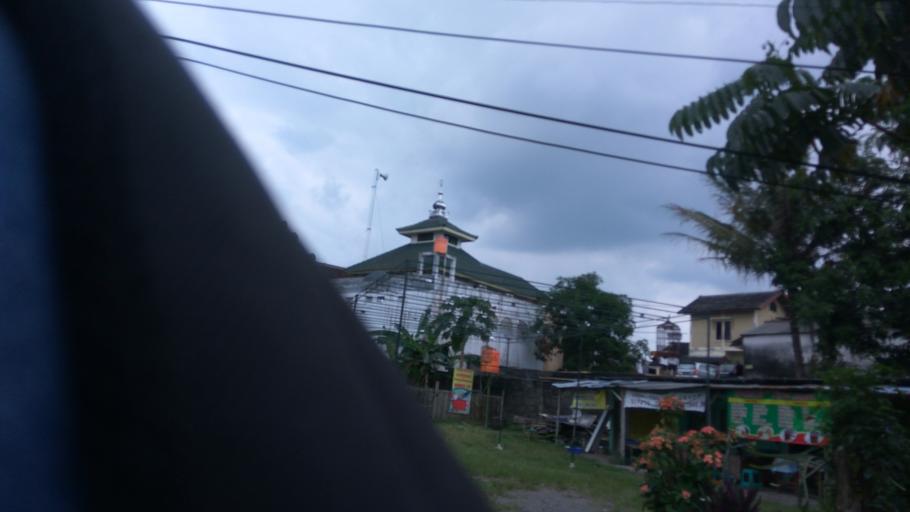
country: ID
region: Daerah Istimewa Yogyakarta
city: Depok
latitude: -7.7396
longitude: 110.4072
